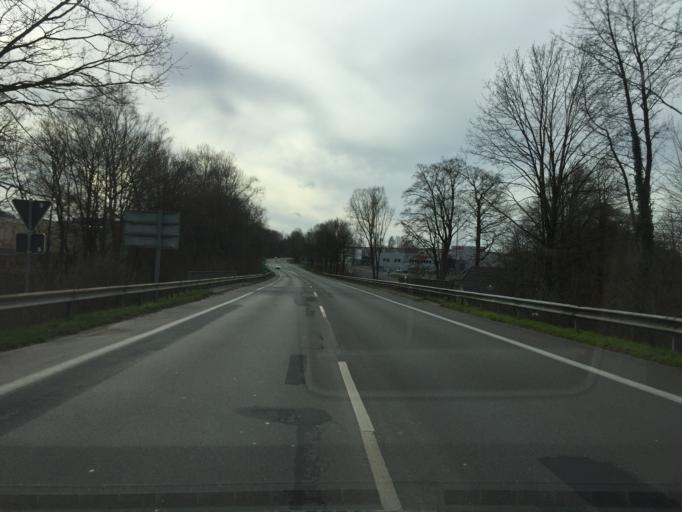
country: DE
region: North Rhine-Westphalia
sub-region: Regierungsbezirk Detmold
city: Vlotho
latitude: 52.1404
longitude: 8.8303
